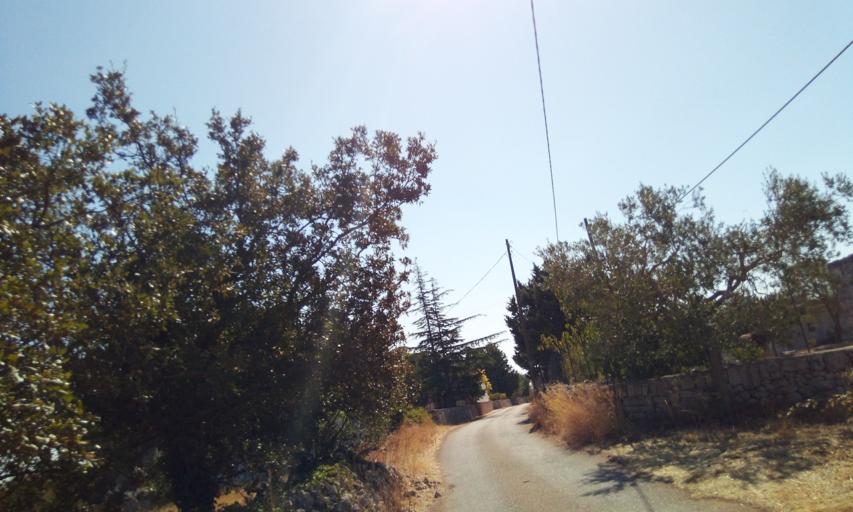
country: IT
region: Apulia
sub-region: Provincia di Bari
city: Gioia del Colle
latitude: 40.8277
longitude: 16.9744
